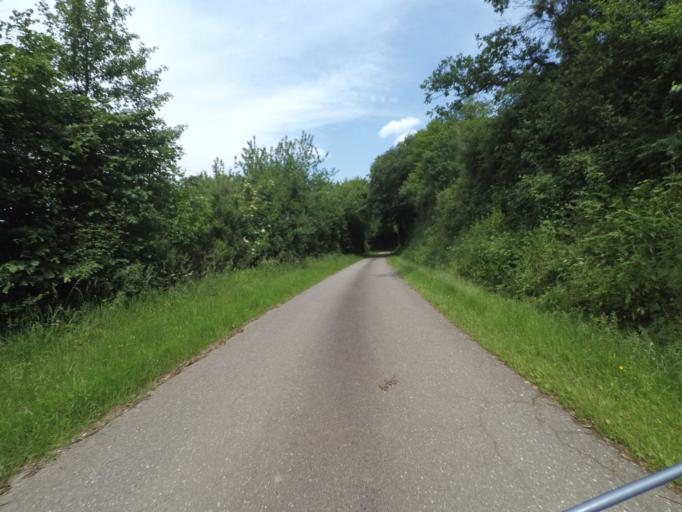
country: DE
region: Rheinland-Pfalz
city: Burgen
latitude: 50.2132
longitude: 7.3972
